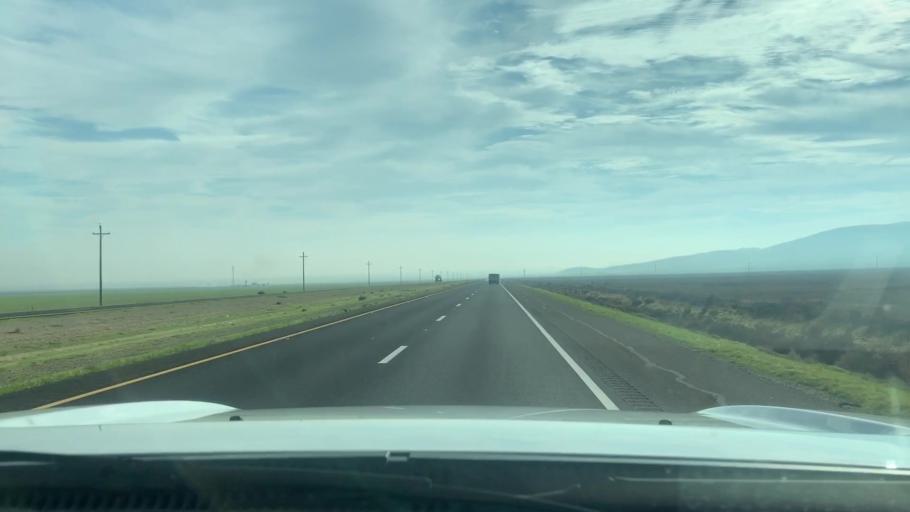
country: US
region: California
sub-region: San Luis Obispo County
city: Shandon
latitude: 35.6625
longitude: -120.0646
